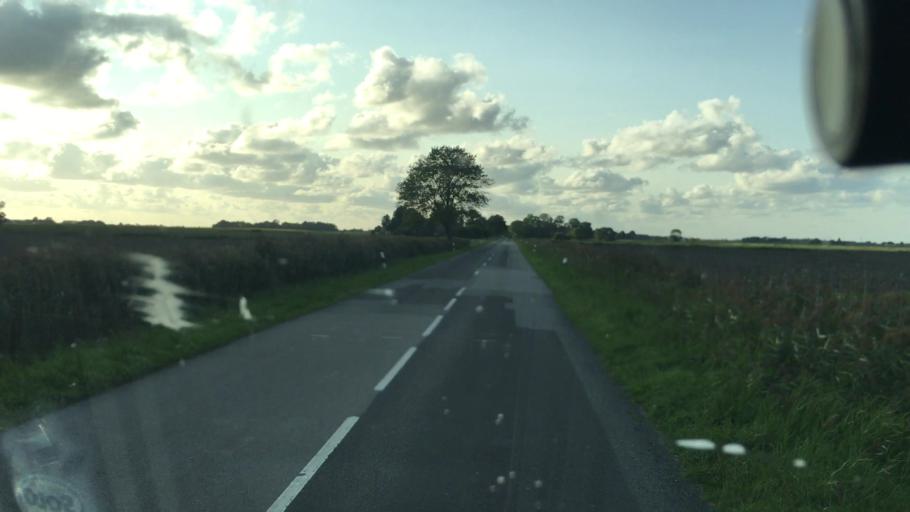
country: DE
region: Lower Saxony
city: Werdum
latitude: 53.6631
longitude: 7.7377
